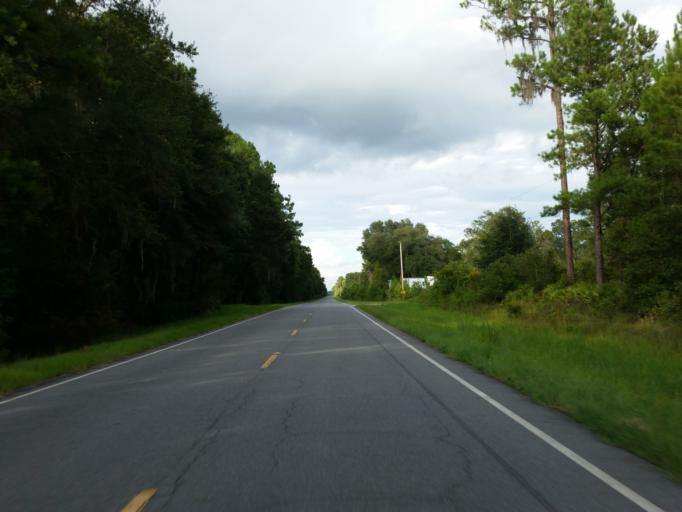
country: US
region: Florida
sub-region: Hamilton County
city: Jasper
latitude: 30.6254
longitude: -82.6103
